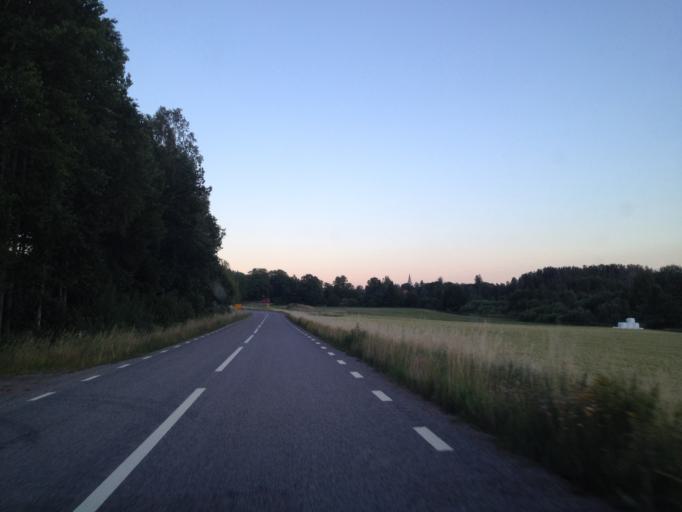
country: SE
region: Kalmar
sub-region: Vasterviks Kommun
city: Overum
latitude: 57.9964
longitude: 16.1795
